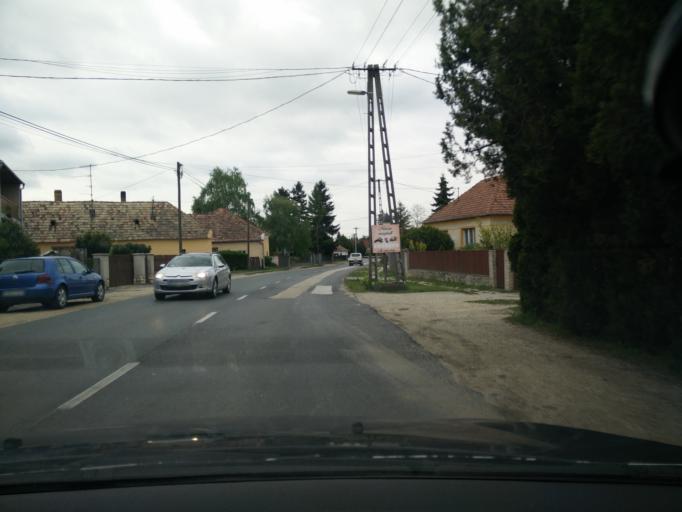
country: HU
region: Veszprem
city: Papa
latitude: 47.3966
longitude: 17.4734
